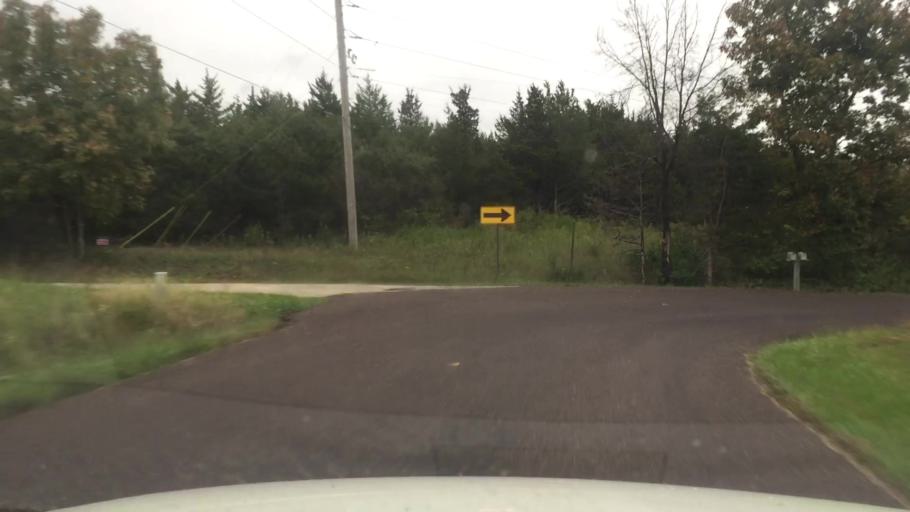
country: US
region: Missouri
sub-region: Boone County
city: Ashland
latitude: 38.8147
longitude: -92.2791
